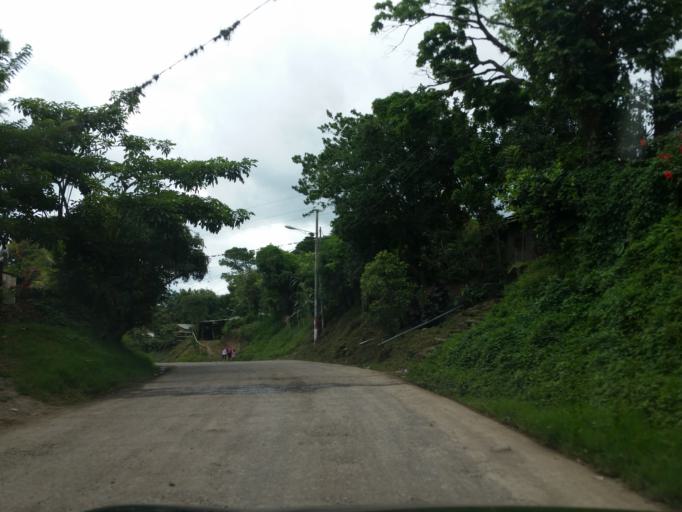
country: NI
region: Matagalpa
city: San Ramon
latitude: 12.9364
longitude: -85.8638
